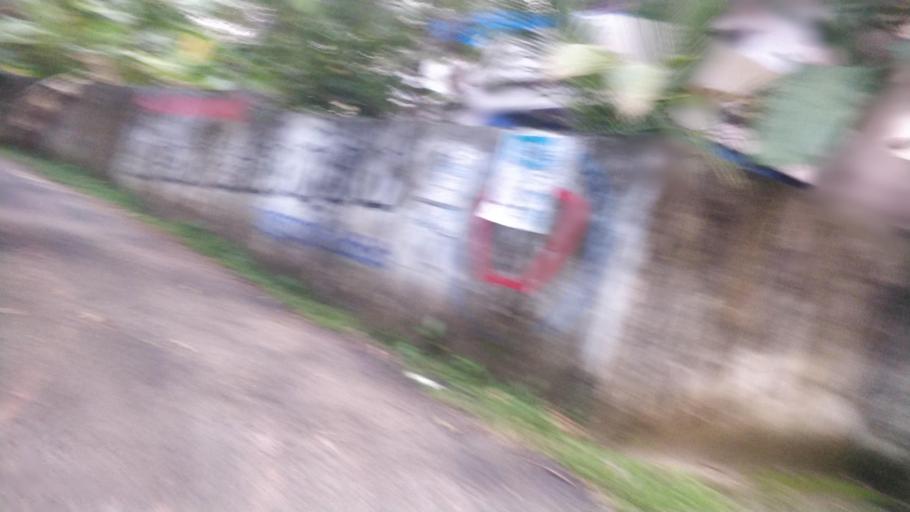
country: IN
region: Kerala
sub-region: Alappuzha
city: Shertallai
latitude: 9.6752
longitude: 76.3345
